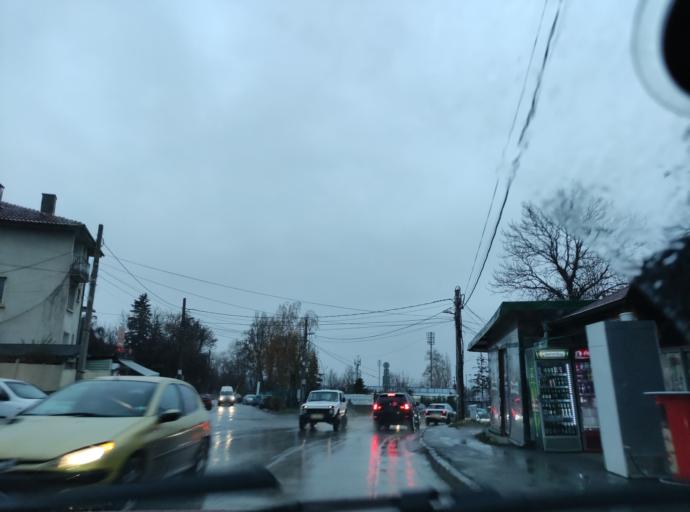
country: BG
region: Sofia-Capital
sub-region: Stolichna Obshtina
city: Sofia
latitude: 42.6341
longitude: 23.3106
